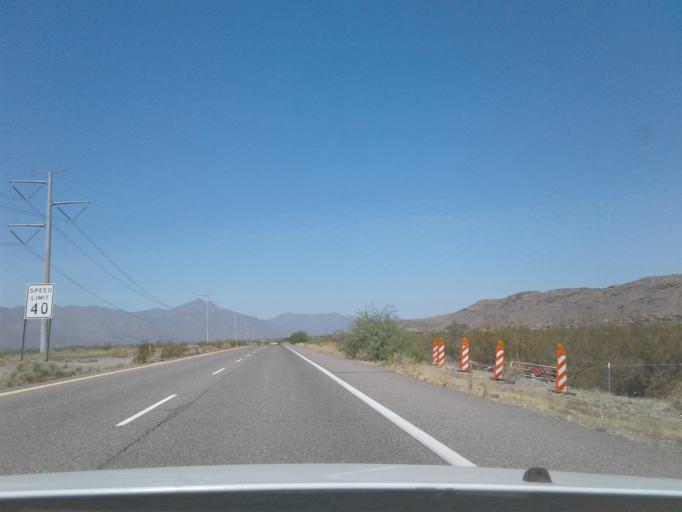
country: US
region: Arizona
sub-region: Maricopa County
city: Laveen
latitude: 33.2911
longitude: -112.1069
